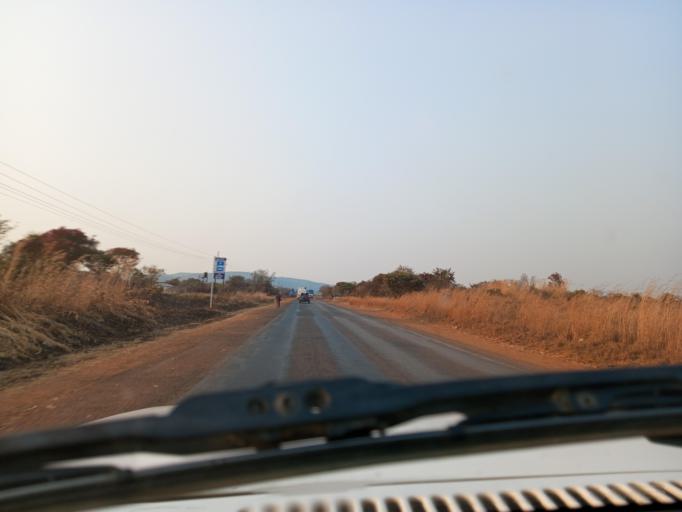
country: ZM
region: Northern
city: Mpika
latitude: -11.9160
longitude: 31.4160
